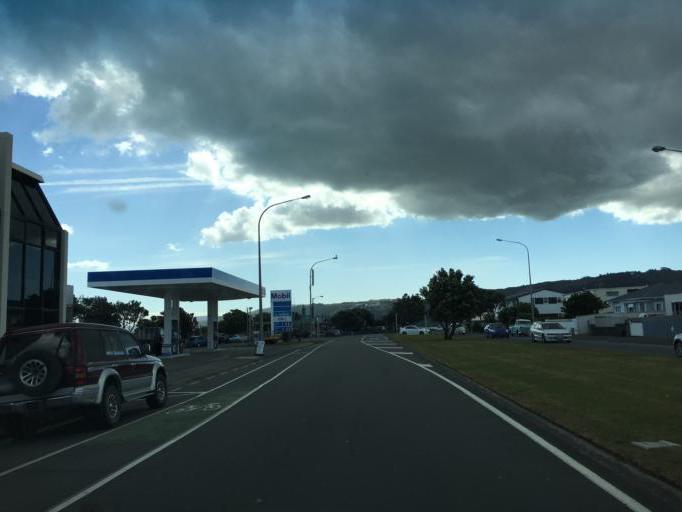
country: NZ
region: Wellington
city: Petone
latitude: -41.2319
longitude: 174.8913
